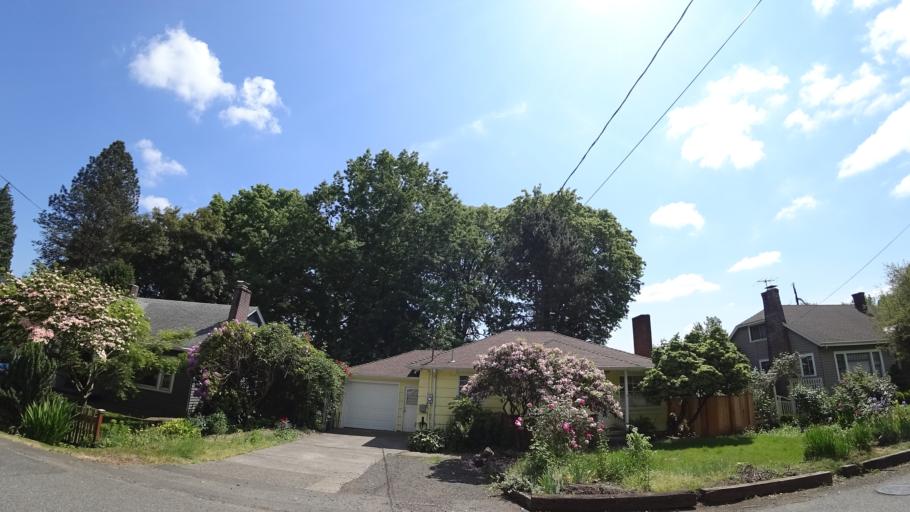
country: US
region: Oregon
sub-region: Clackamas County
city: Lake Oswego
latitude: 45.4683
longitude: -122.7012
